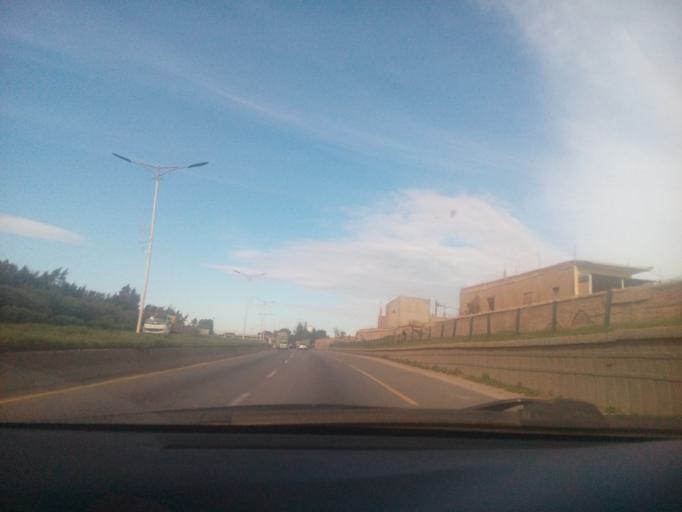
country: DZ
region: Oran
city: Es Senia
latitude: 35.6088
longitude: -0.5781
